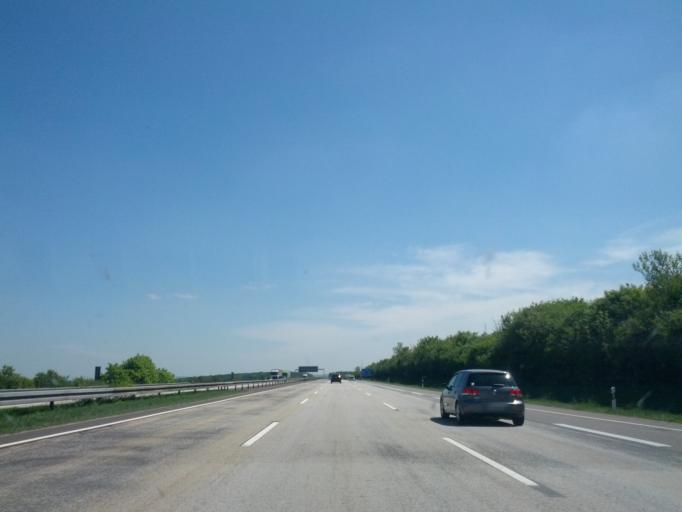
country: DE
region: Thuringia
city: Troistedt
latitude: 50.9491
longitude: 11.2480
